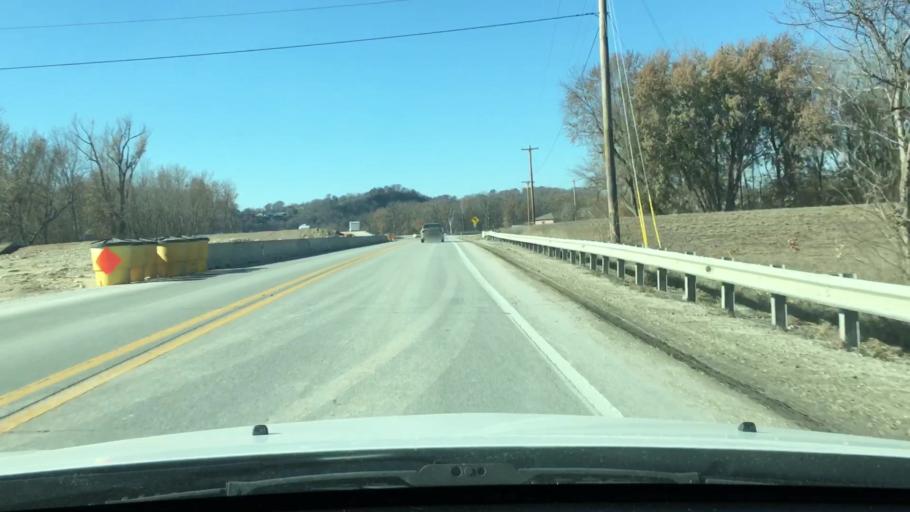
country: US
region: Missouri
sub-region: Pike County
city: Louisiana
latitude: 39.4600
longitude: -91.0365
